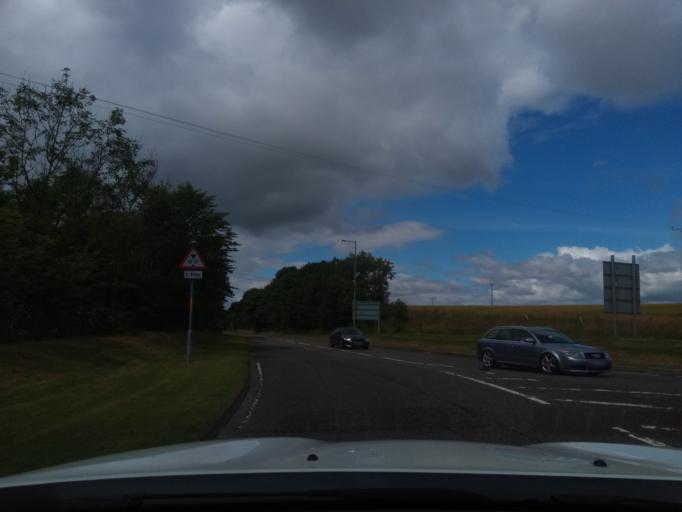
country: GB
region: Scotland
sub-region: Fife
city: Oakley
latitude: 56.0595
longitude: -3.5458
